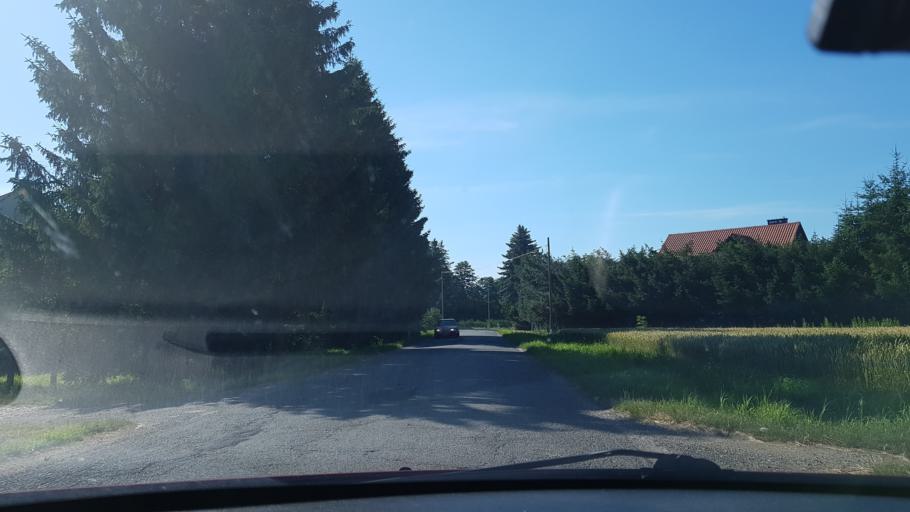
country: PL
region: Lower Silesian Voivodeship
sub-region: Powiat klodzki
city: Bystrzyca Klodzka
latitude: 50.2636
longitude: 16.6656
